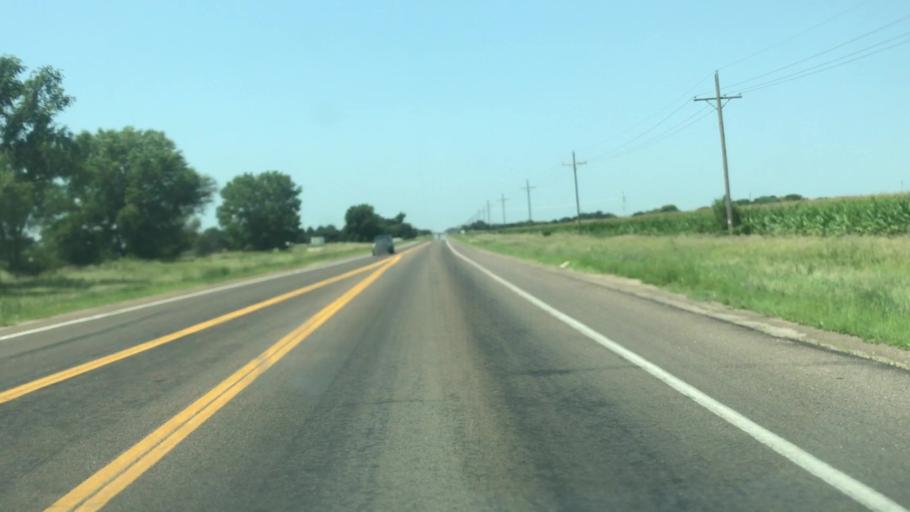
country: US
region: Nebraska
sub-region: Hall County
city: Grand Island
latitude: 40.8869
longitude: -98.3224
